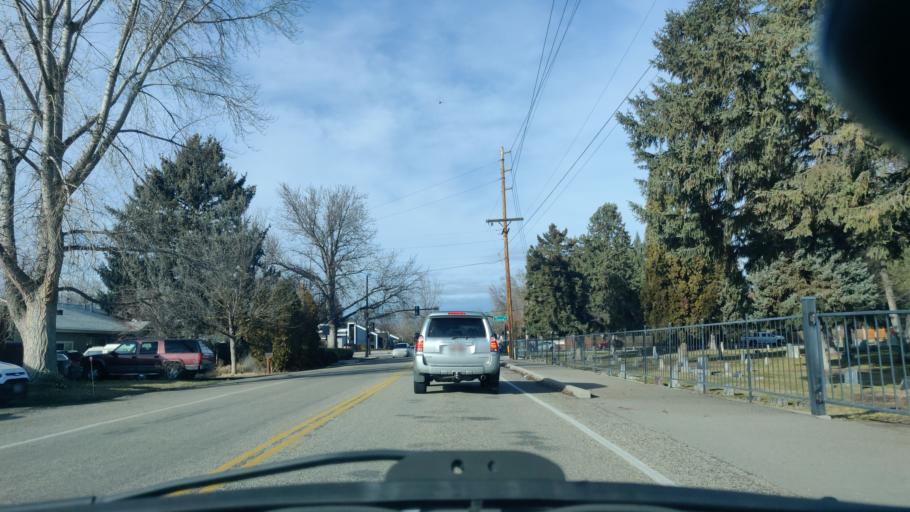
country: US
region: Idaho
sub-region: Ada County
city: Garden City
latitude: 43.6106
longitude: -116.2335
